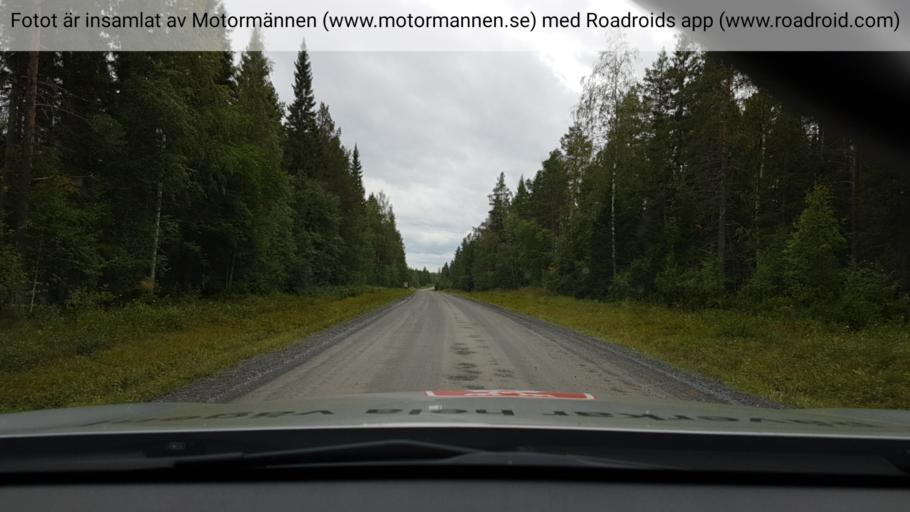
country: SE
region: Vaesterbotten
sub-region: Skelleftea Kommun
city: Forsbacka
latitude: 64.8267
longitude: 20.4979
